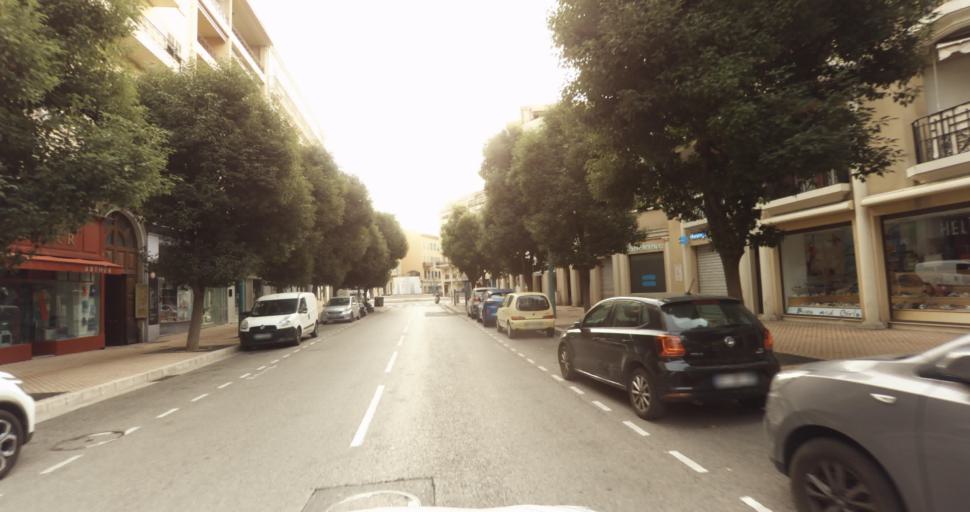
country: FR
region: Provence-Alpes-Cote d'Azur
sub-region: Departement des Alpes-Maritimes
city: Menton
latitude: 43.7739
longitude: 7.5005
